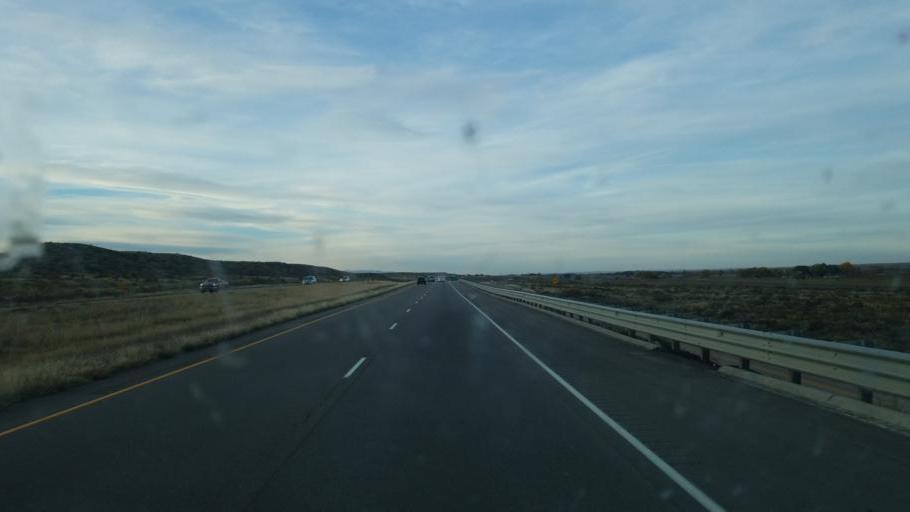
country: US
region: Colorado
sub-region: Pueblo County
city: Pueblo West
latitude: 38.4761
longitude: -104.6153
